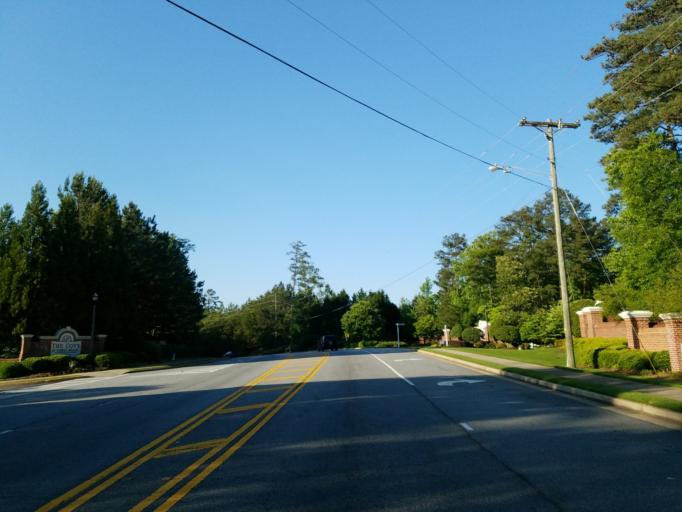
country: US
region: Georgia
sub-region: Cobb County
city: Mableton
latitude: 33.8370
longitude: -84.5359
